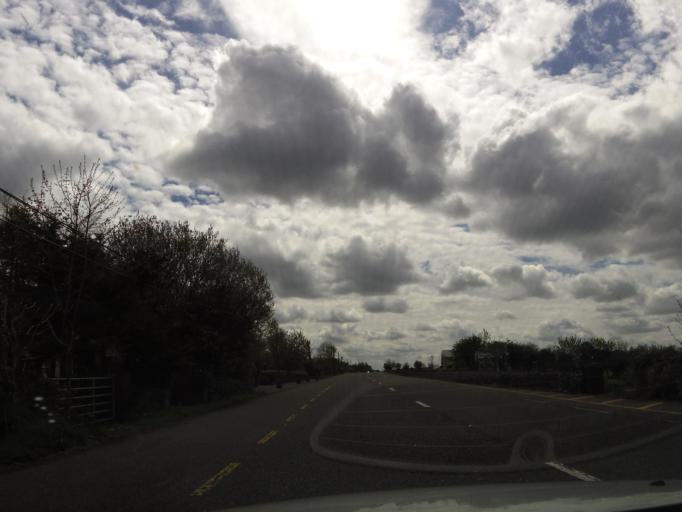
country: IE
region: Connaught
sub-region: County Galway
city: Tuam
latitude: 53.5553
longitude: -8.8423
